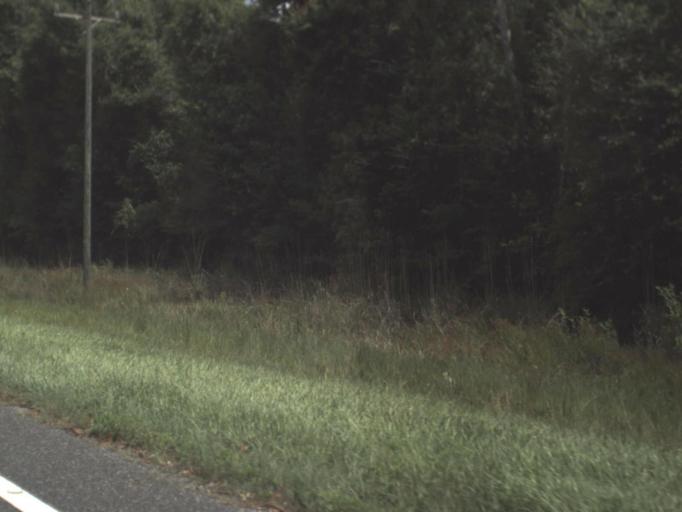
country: US
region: Florida
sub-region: Taylor County
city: Perry
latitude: 29.9565
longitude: -83.4636
